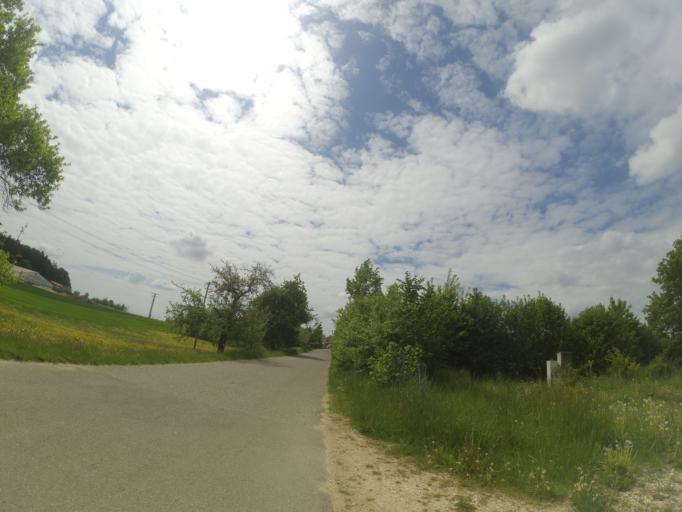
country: DE
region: Baden-Wuerttemberg
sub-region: Tuebingen Region
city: Blaubeuren
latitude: 48.4343
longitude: 9.7743
